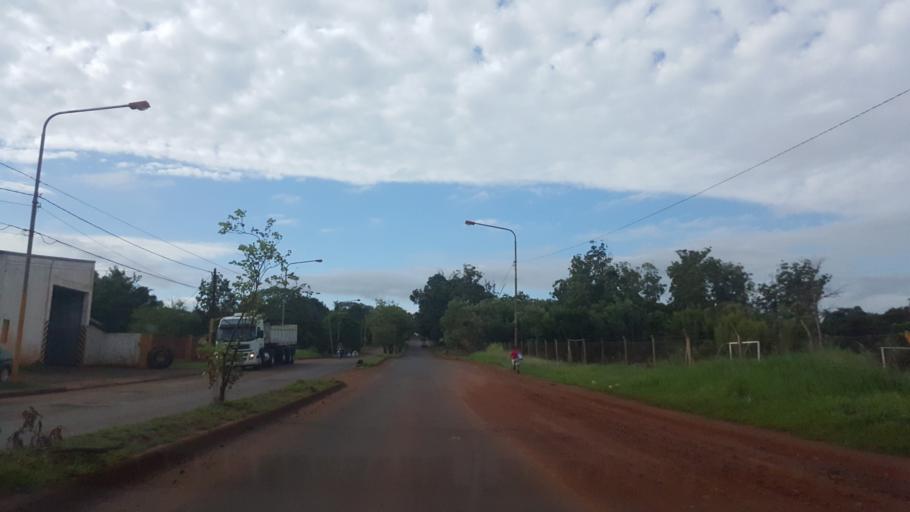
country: AR
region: Misiones
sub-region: Departamento de Capital
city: Posadas
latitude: -27.3933
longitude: -55.9353
